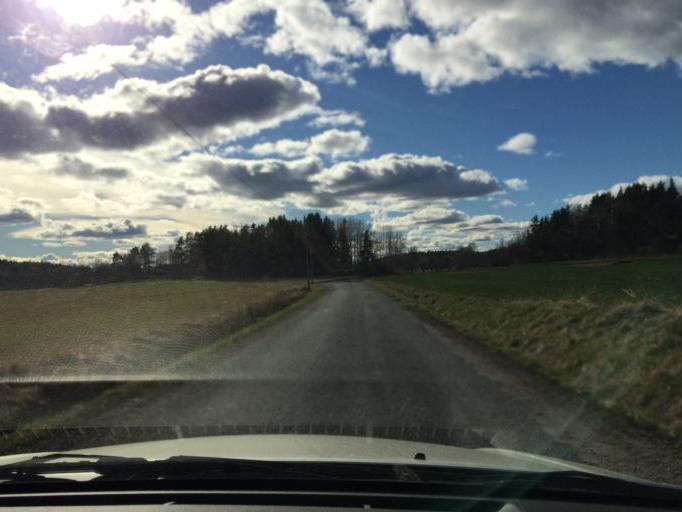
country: SE
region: Soedermanland
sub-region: Eskilstuna Kommun
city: Hallbybrunn
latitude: 59.4296
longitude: 16.4016
